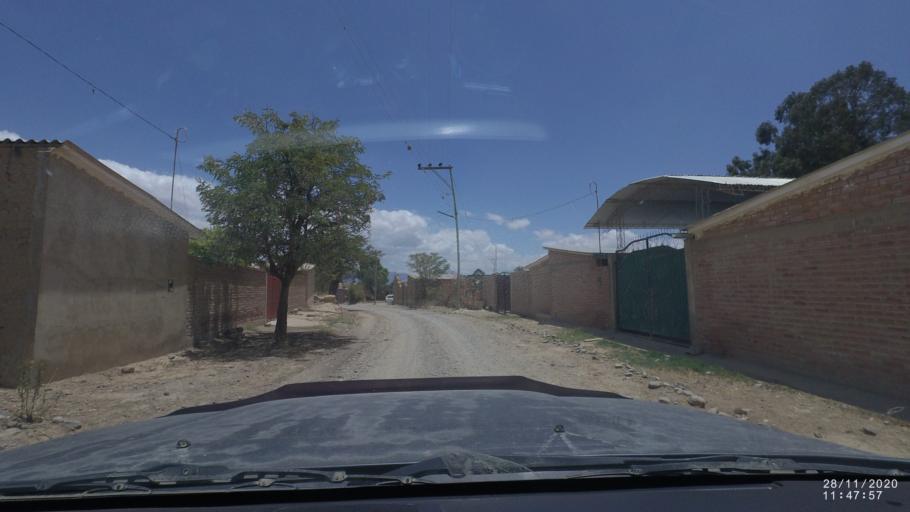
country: BO
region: Cochabamba
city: Tarata
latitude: -17.6421
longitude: -66.0334
